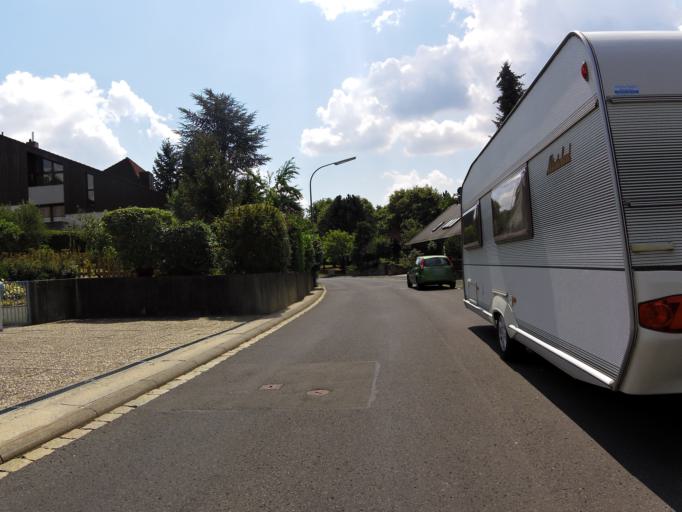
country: DE
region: Bavaria
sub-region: Regierungsbezirk Unterfranken
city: Randersacker
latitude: 49.7492
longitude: 9.9523
